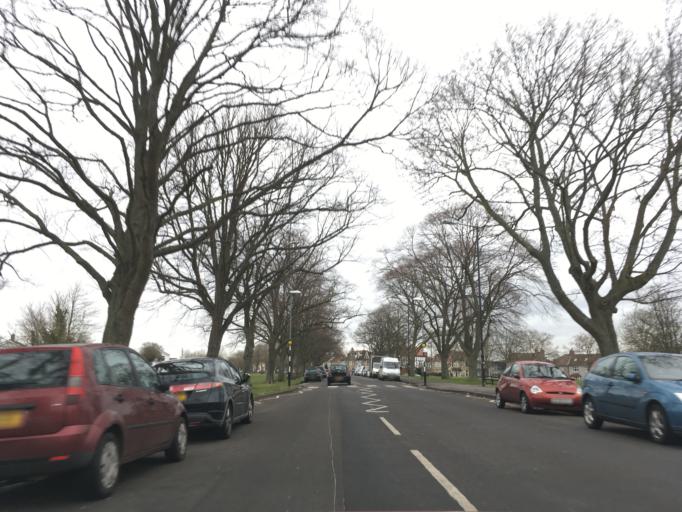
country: GB
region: England
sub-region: Bristol
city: Bristol
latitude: 51.4897
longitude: -2.5876
